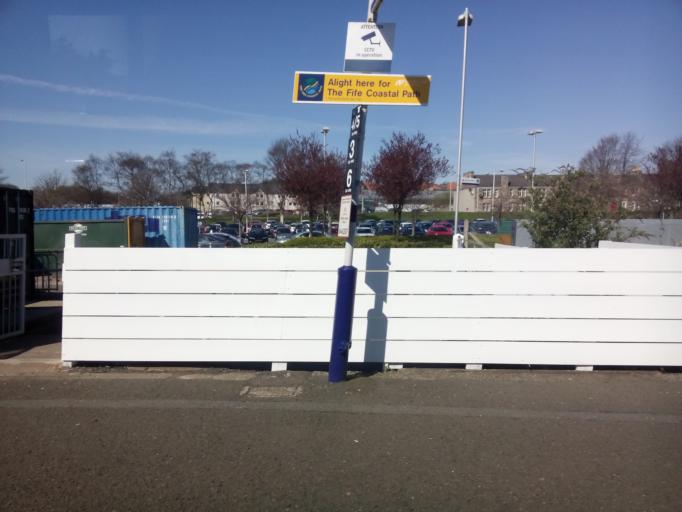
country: GB
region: Scotland
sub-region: Fife
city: Kirkcaldy
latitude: 56.1122
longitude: -3.1670
